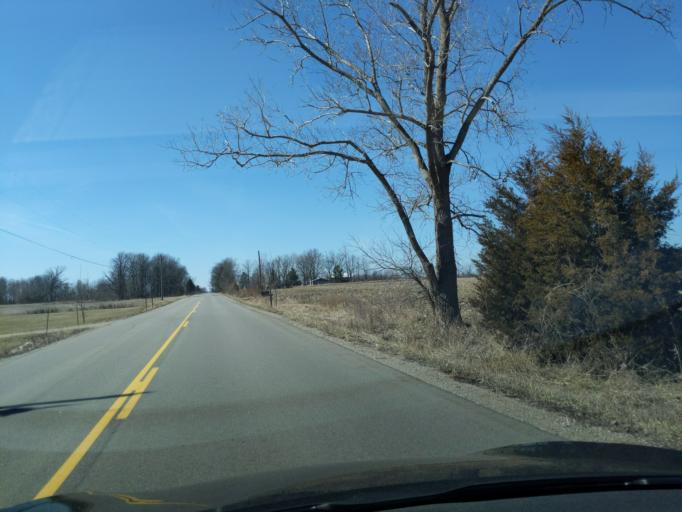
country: US
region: Michigan
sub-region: Eaton County
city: Grand Ledge
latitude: 42.7266
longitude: -84.8387
